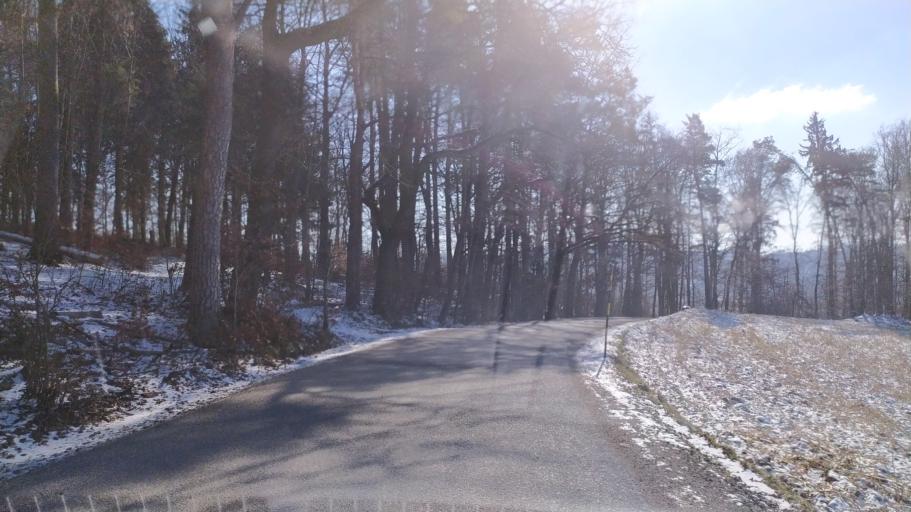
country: AT
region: Upper Austria
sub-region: Politischer Bezirk Urfahr-Umgebung
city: Ottensheim
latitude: 48.3409
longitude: 14.1938
